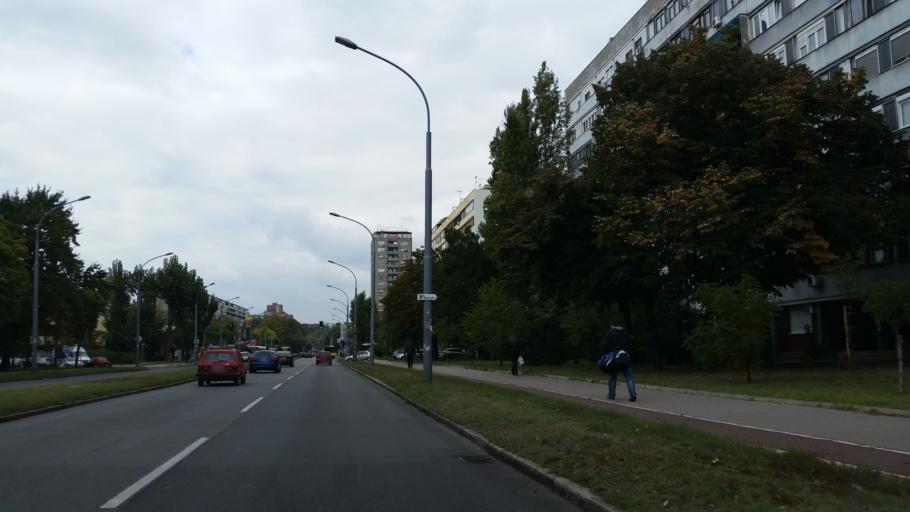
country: RS
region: Central Serbia
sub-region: Belgrade
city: Zemun
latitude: 44.8251
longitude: 20.4113
